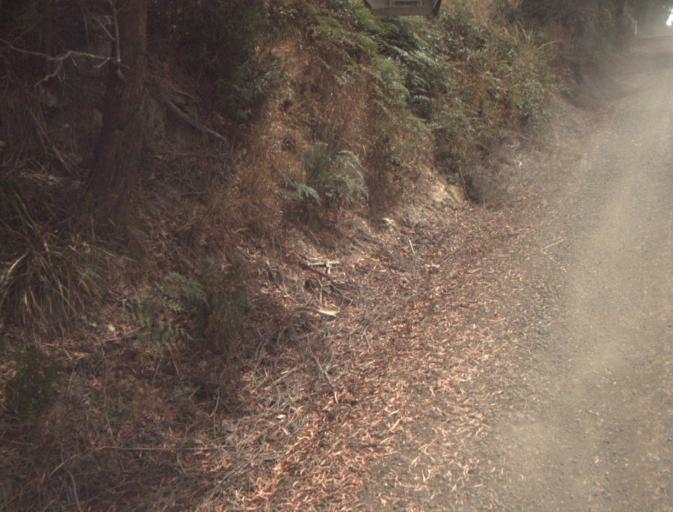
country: AU
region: Tasmania
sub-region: Launceston
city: Mayfield
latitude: -41.2083
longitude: 147.1400
